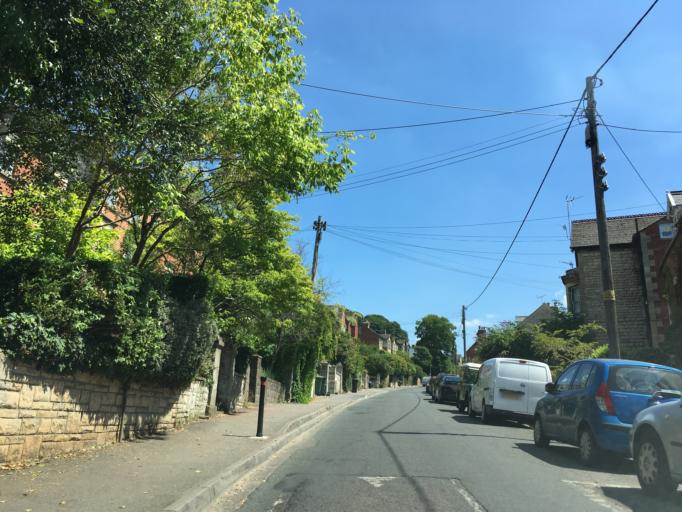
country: GB
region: England
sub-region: Gloucestershire
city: Stroud
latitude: 51.7437
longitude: -2.2064
